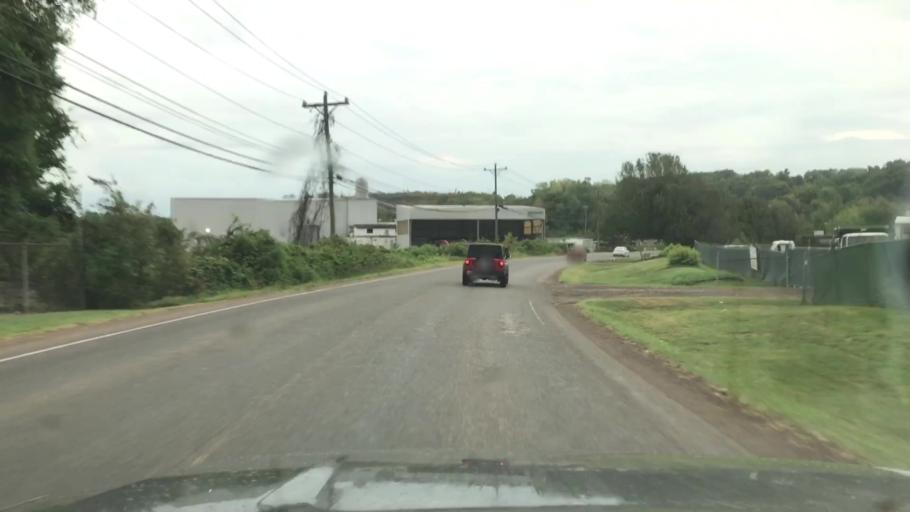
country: US
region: Tennessee
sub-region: Davidson County
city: Lakewood
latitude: 36.1846
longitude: -86.6250
